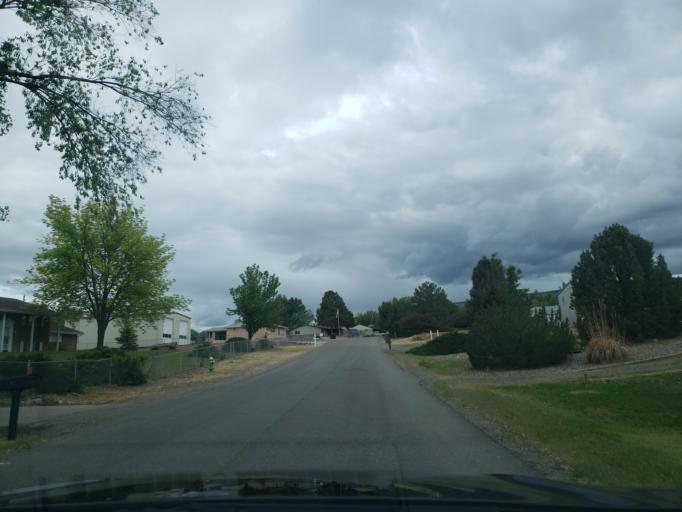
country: US
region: Colorado
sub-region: Mesa County
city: Redlands
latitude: 39.1005
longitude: -108.6616
